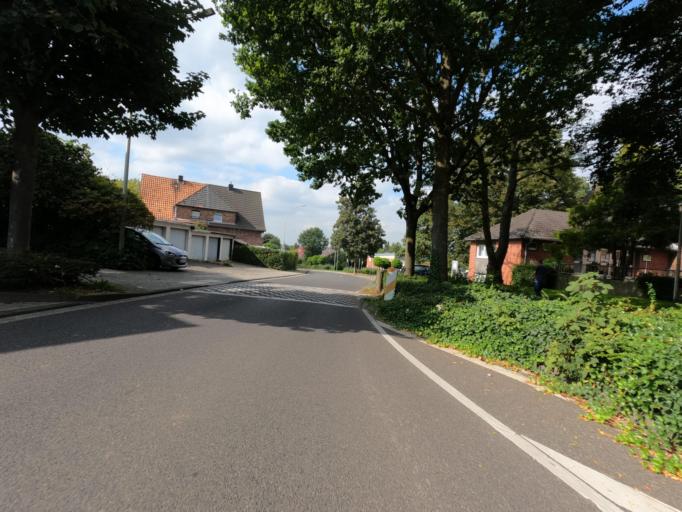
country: DE
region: North Rhine-Westphalia
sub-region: Regierungsbezirk Koln
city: Ubach-Palenberg
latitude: 50.9409
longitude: 6.1099
